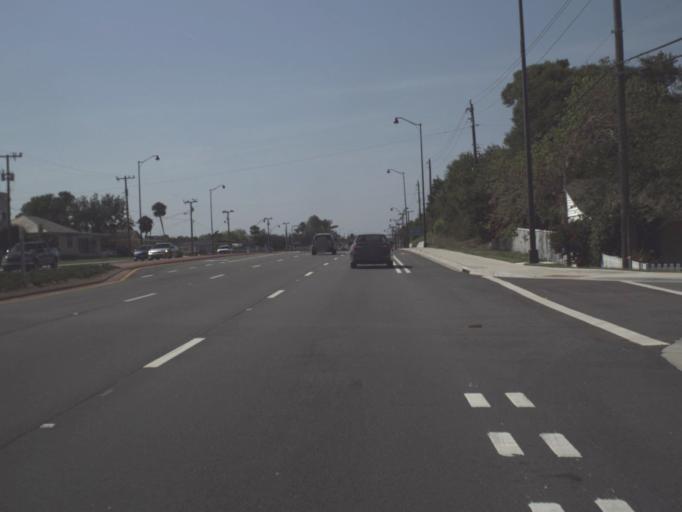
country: US
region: Florida
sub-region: Brevard County
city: Cocoa
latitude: 28.3870
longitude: -80.7442
